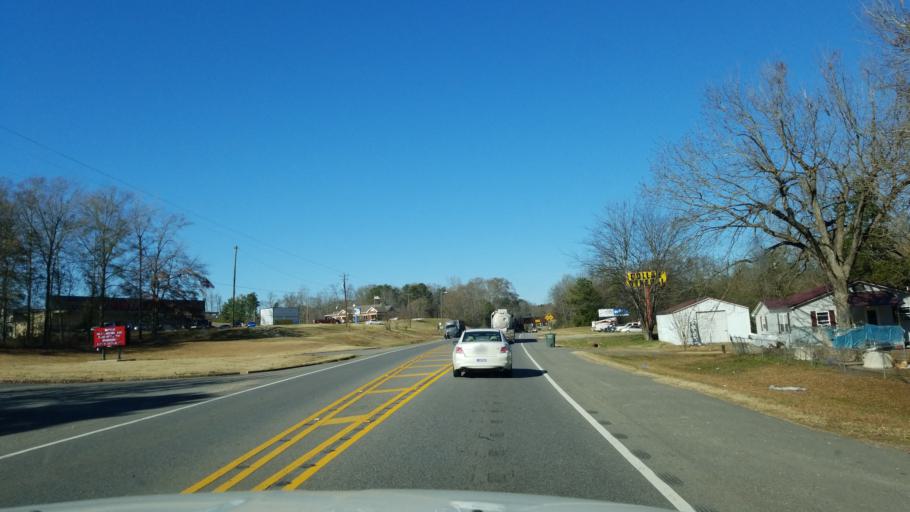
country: US
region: Alabama
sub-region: Pickens County
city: Gordo
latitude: 33.3205
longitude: -87.9089
